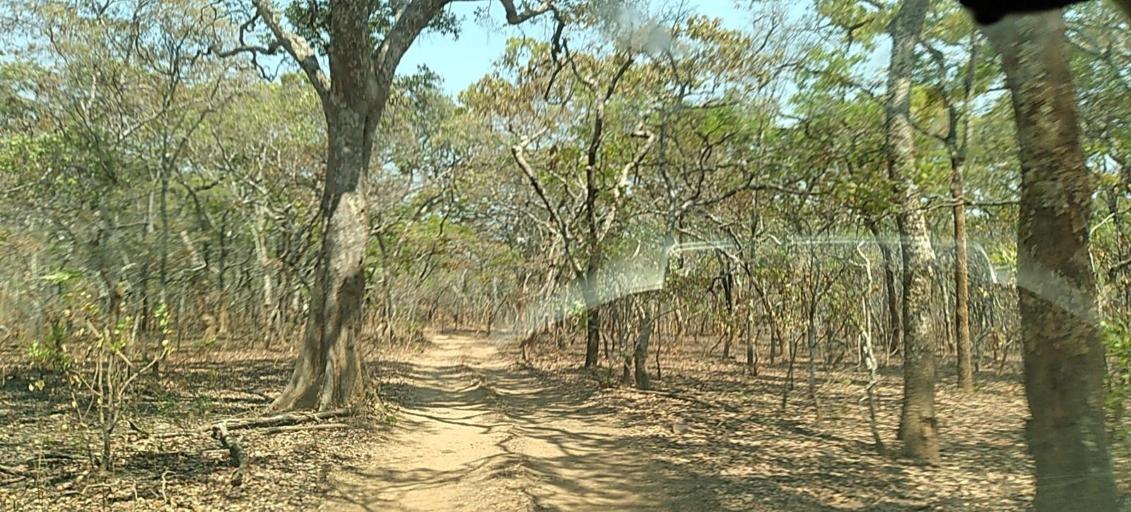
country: ZM
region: North-Western
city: Kasempa
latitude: -13.3936
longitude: 25.5951
